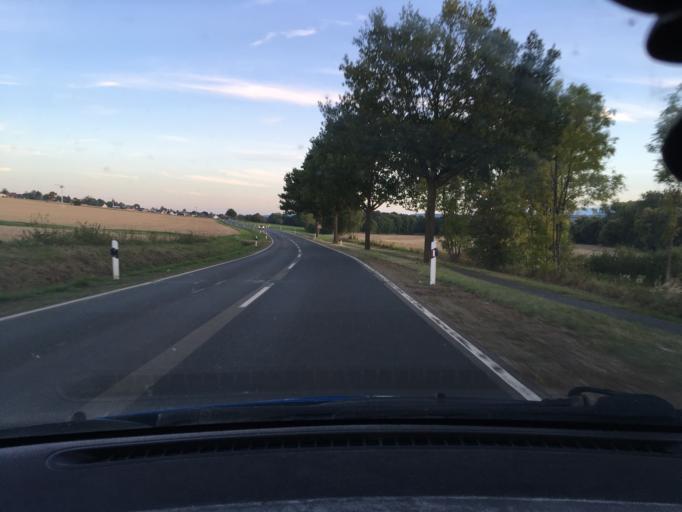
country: DE
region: Lower Saxony
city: Lauenau
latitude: 52.2883
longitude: 9.3603
